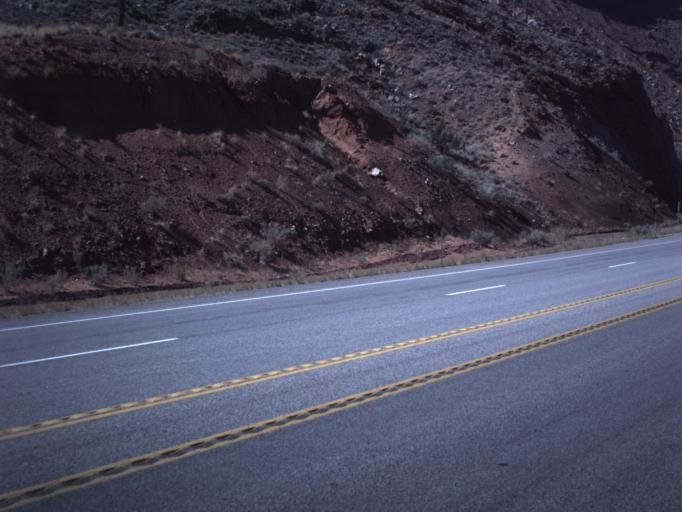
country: US
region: Utah
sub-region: Grand County
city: Moab
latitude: 38.6154
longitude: -109.6184
